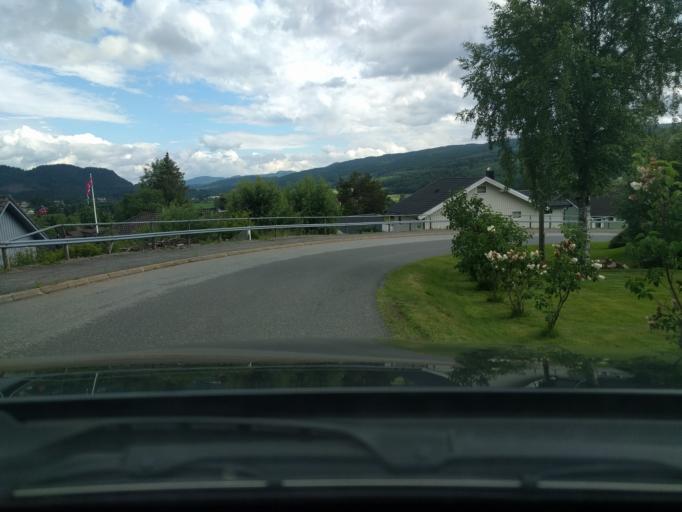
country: NO
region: Telemark
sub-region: Siljan
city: Siljan
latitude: 59.2917
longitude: 9.7127
